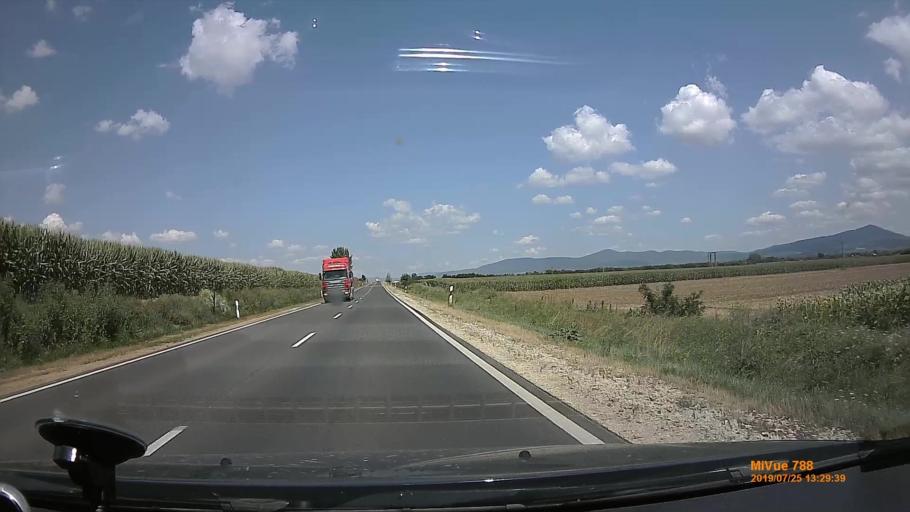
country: HU
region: Borsod-Abauj-Zemplen
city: Encs
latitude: 48.3454
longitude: 21.1192
